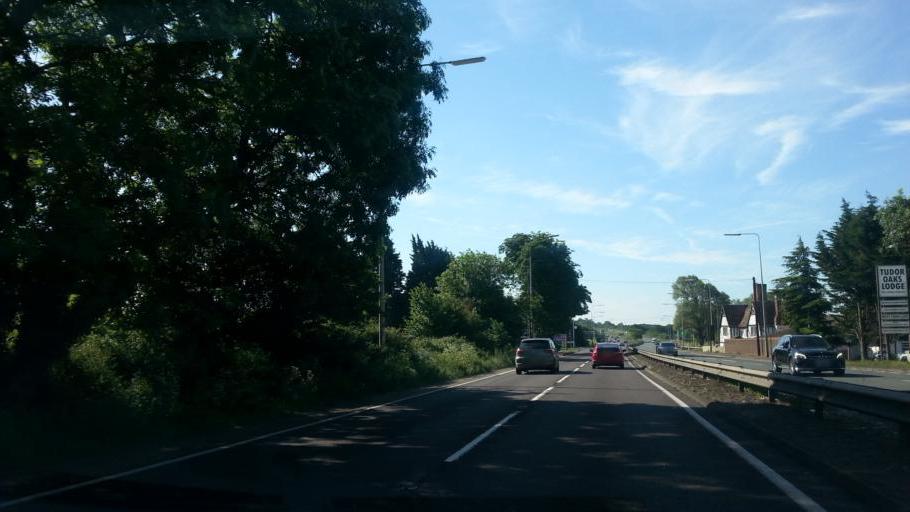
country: GB
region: England
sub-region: Central Bedfordshire
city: Astwick
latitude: 52.0312
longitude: -0.2157
